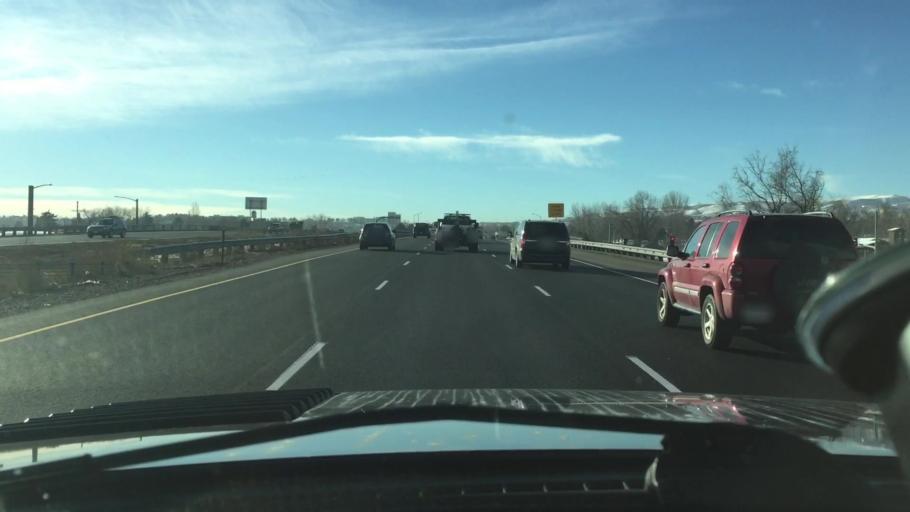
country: US
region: Colorado
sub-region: Jefferson County
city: Applewood
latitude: 39.7628
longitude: -105.1433
